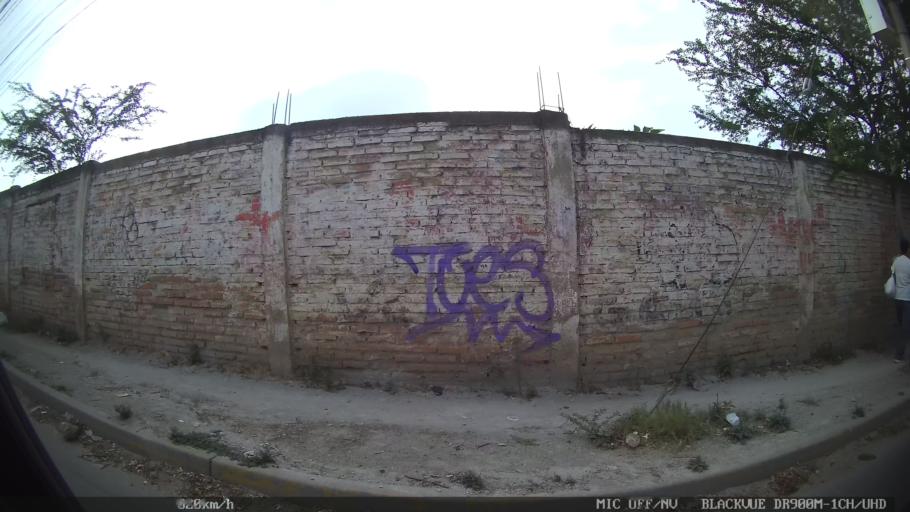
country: MX
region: Jalisco
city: Tonala
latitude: 20.6258
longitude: -103.2360
